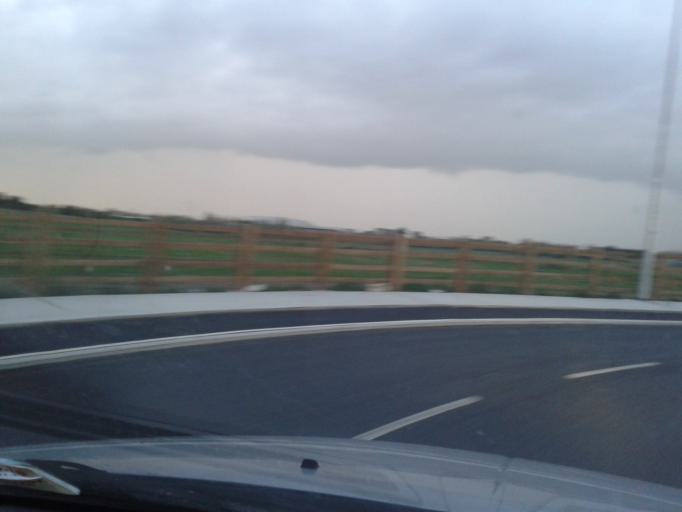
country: IE
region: Leinster
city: Kinsealy-Drinan
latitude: 53.4472
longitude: -6.2127
